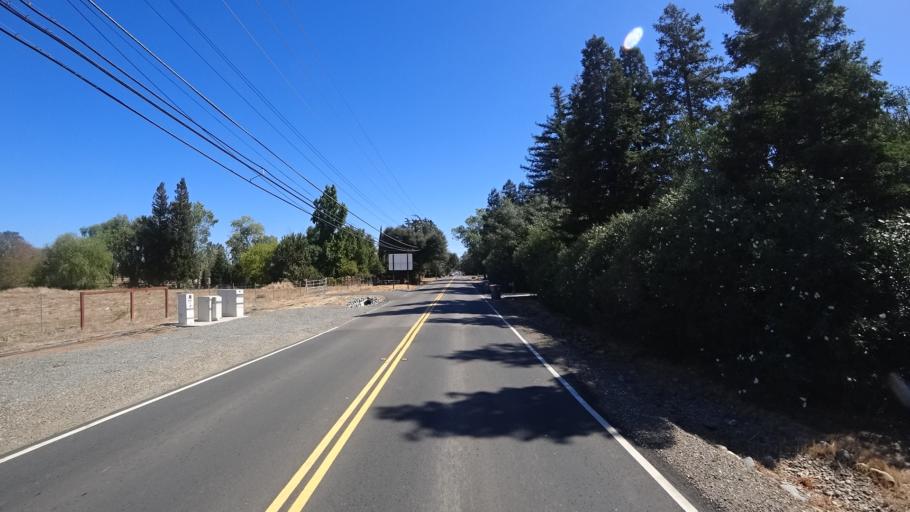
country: US
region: California
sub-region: Sacramento County
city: Vineyard
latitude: 38.4381
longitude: -121.3331
